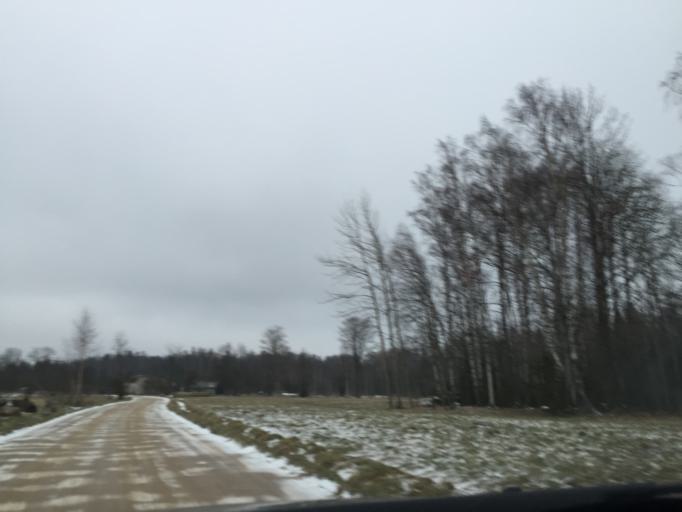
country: LV
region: Saulkrastu
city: Saulkrasti
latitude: 57.5054
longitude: 24.3824
